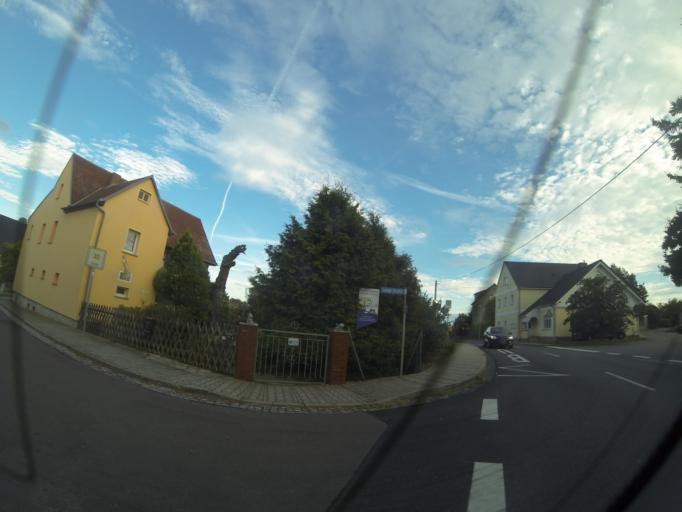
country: DE
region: Thuringia
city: Schmolln
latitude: 50.9129
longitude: 12.3494
